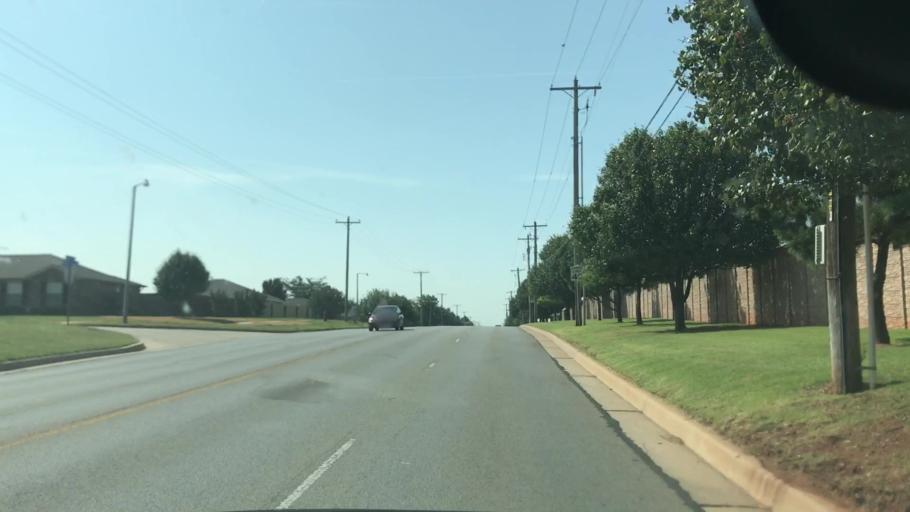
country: US
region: Oklahoma
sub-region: Cleveland County
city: Moore
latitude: 35.3561
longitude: -97.5122
